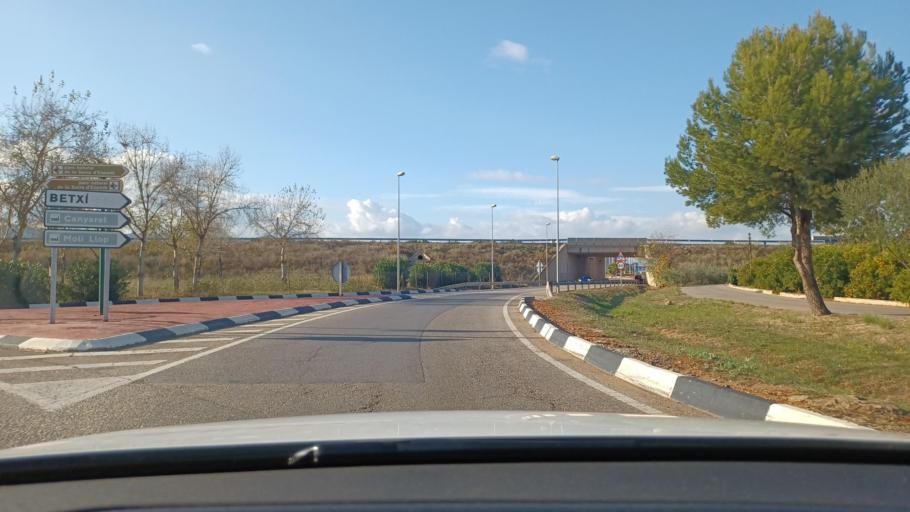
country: ES
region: Valencia
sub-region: Provincia de Castello
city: Betxi
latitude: 39.9257
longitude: -0.1897
